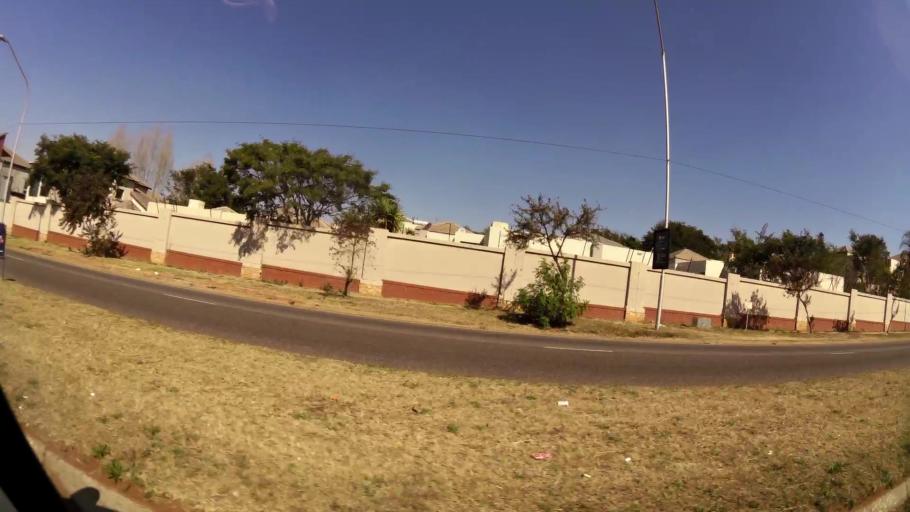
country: ZA
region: Gauteng
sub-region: City of Tshwane Metropolitan Municipality
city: Pretoria
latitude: -25.7652
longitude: 28.2697
